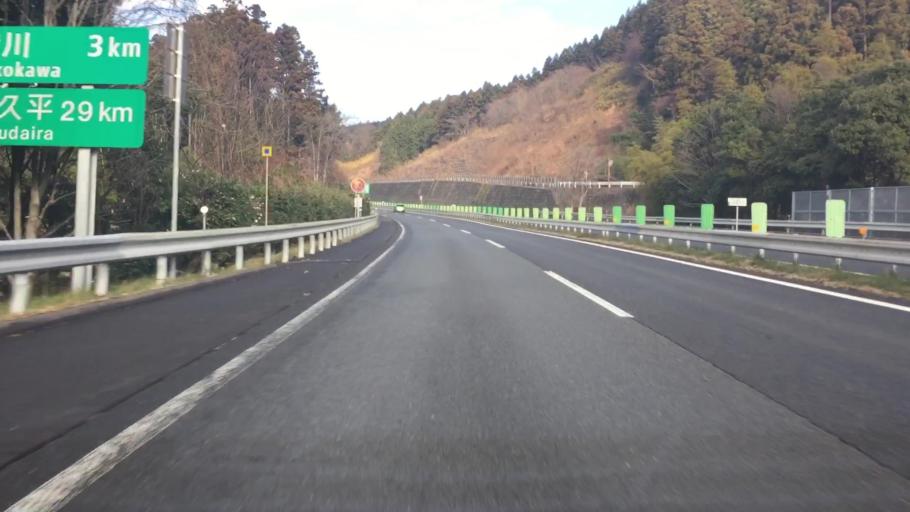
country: JP
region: Gunma
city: Annaka
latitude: 36.3227
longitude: 138.7709
